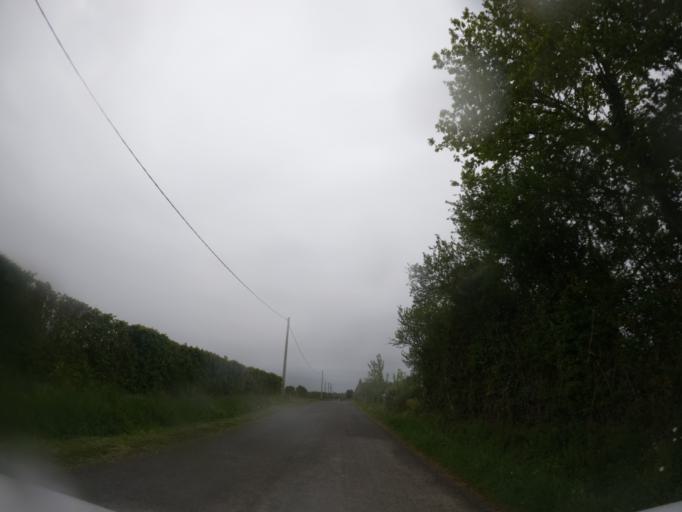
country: FR
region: Brittany
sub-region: Departement d'Ille-et-Vilaine
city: Argentre-du-Plessis
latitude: 47.9578
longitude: -1.1279
